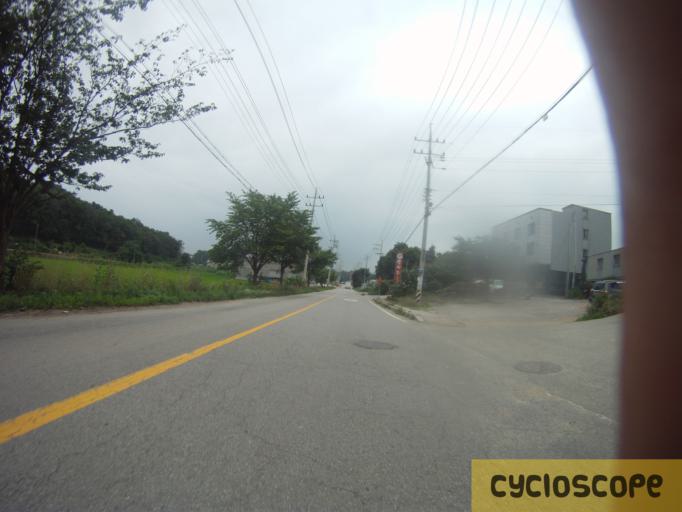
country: KR
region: Gyeonggi-do
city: Hwaseong-si
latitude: 37.1656
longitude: 126.9325
